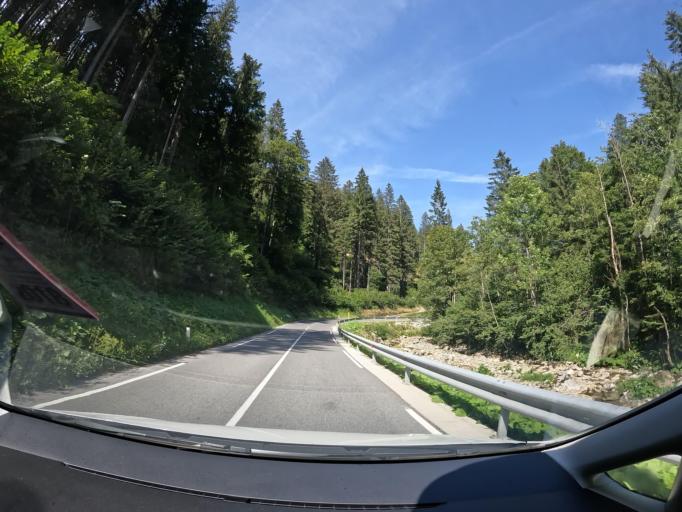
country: SI
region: Zirovnica
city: Zirovnica
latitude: 46.4425
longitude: 14.1703
